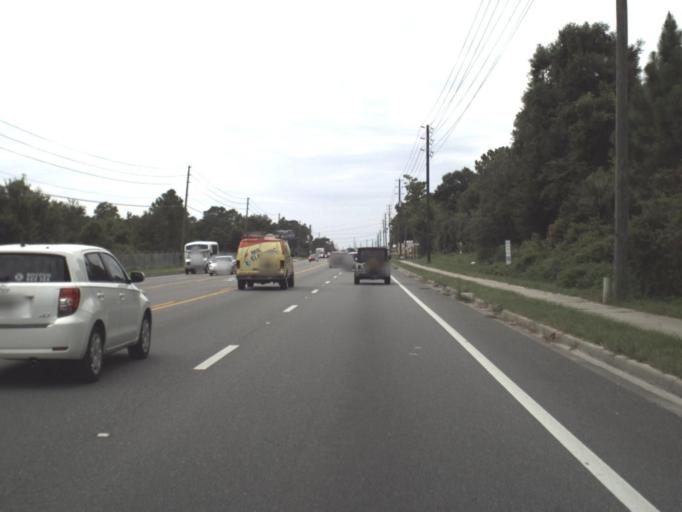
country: US
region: Florida
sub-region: Citrus County
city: Crystal River
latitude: 28.8947
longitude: -82.5549
